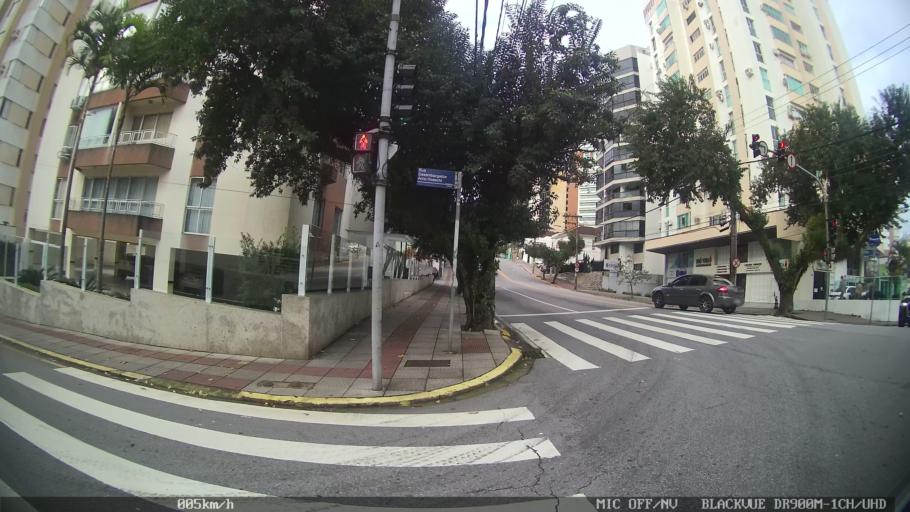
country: BR
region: Santa Catarina
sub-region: Florianopolis
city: Florianopolis
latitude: -27.5922
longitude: -48.5568
